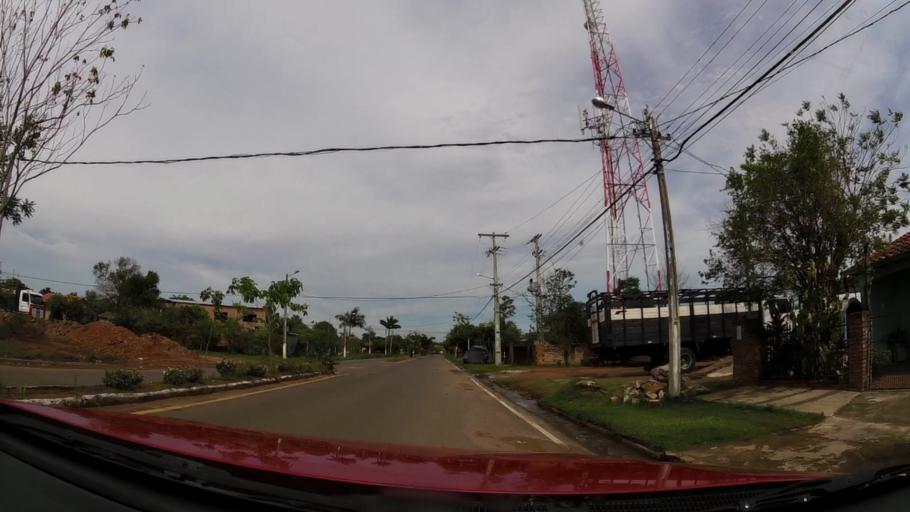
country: PY
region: Central
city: Limpio
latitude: -25.1757
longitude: -57.4789
